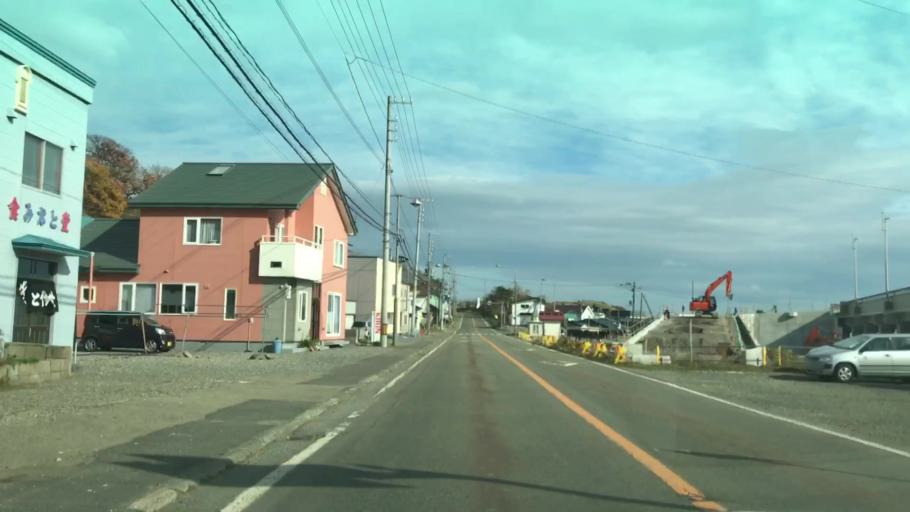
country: JP
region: Hokkaido
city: Obihiro
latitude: 42.0436
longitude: 143.2943
